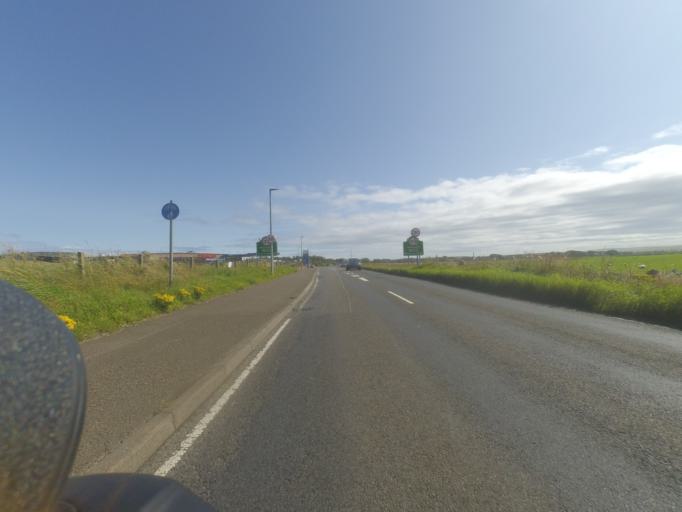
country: GB
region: Scotland
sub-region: Highland
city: Wick
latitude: 58.4527
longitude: -3.1017
